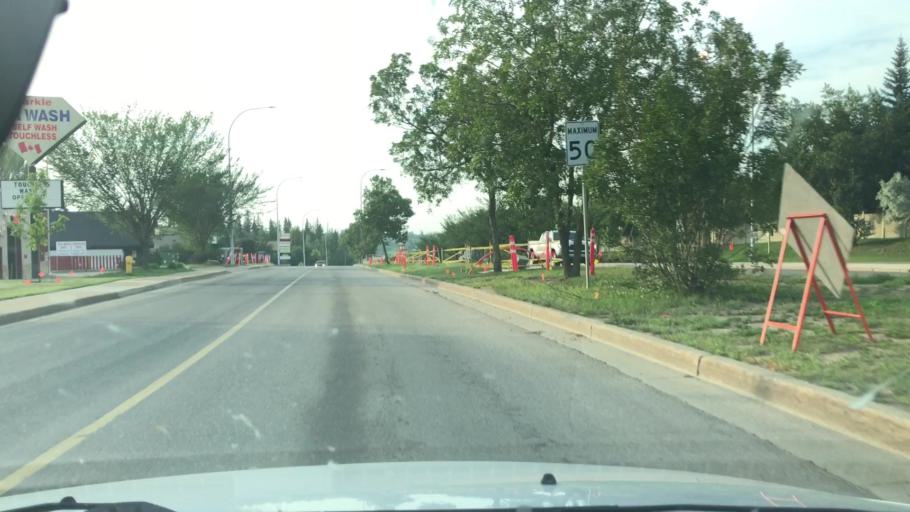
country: CA
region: Alberta
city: St. Albert
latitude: 53.6281
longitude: -113.6197
